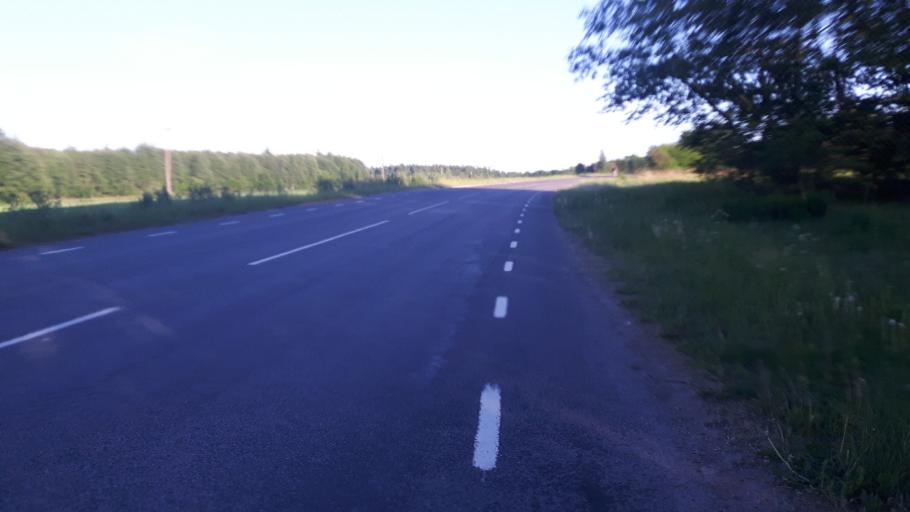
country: EE
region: Raplamaa
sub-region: Jaervakandi vald
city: Jarvakandi
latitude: 58.7812
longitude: 24.9426
